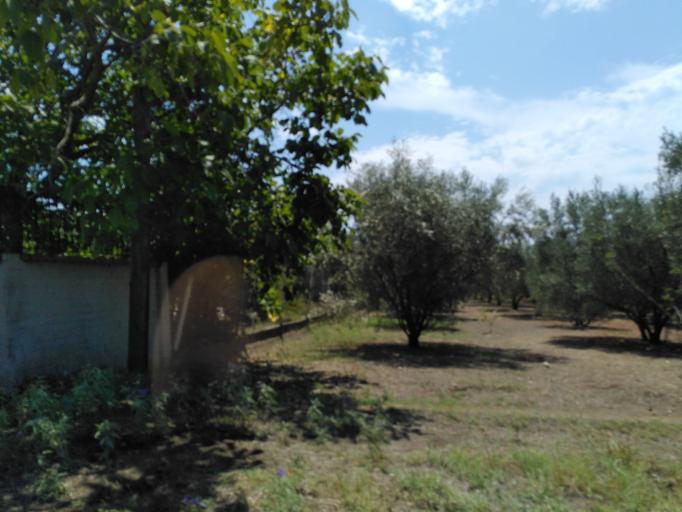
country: GR
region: Central Macedonia
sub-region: Nomos Thessalonikis
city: Epanomi
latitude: 40.4316
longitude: 22.8913
